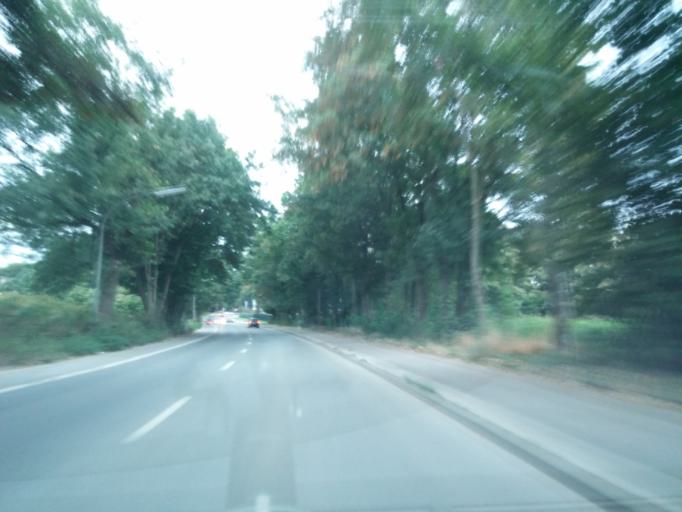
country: DE
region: North Rhine-Westphalia
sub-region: Regierungsbezirk Munster
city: Gladbeck
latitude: 51.5701
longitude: 7.0298
